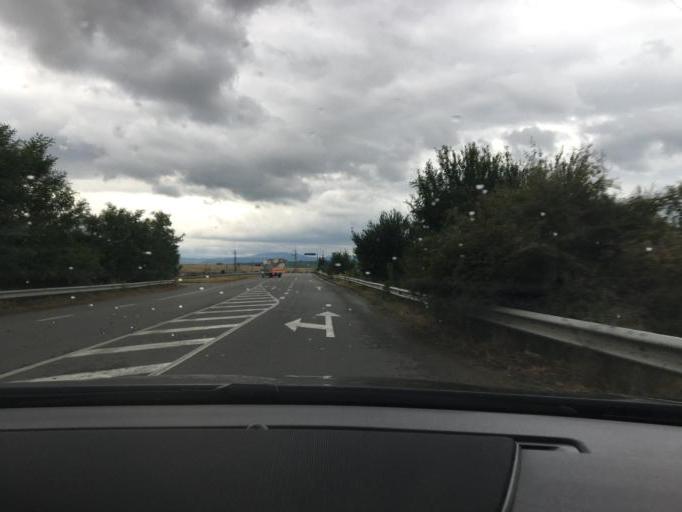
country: BG
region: Kyustendil
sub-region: Obshtina Kyustendil
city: Kyustendil
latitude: 42.2928
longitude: 22.7203
